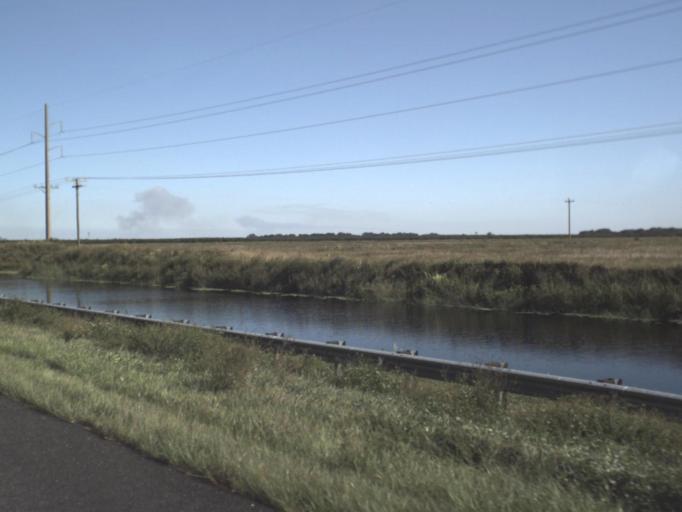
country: US
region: Florida
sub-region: Glades County
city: Moore Haven
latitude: 26.7532
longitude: -81.0982
